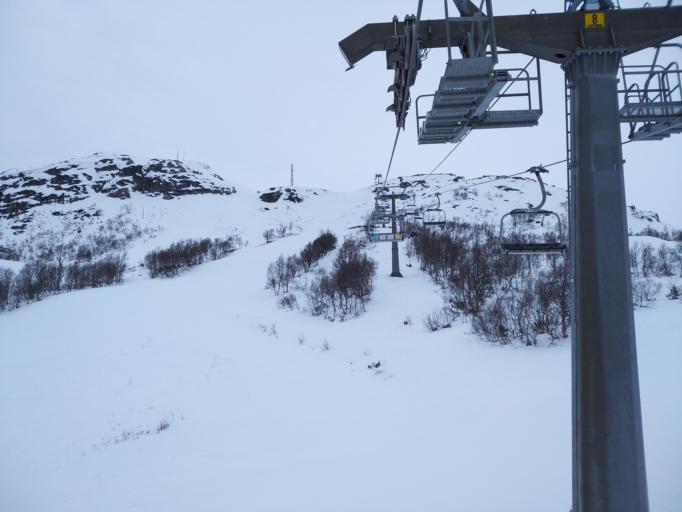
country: NO
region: Aust-Agder
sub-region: Bykle
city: Hovden
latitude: 59.5752
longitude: 7.3395
